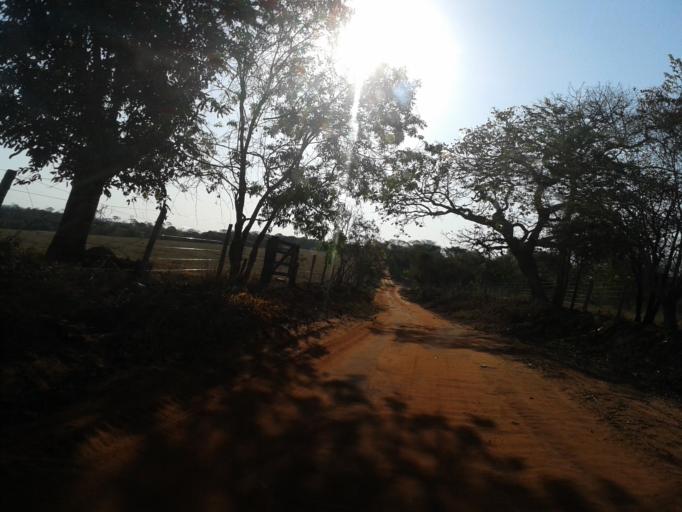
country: BR
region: Minas Gerais
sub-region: Campina Verde
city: Campina Verde
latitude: -19.2545
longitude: -49.5735
